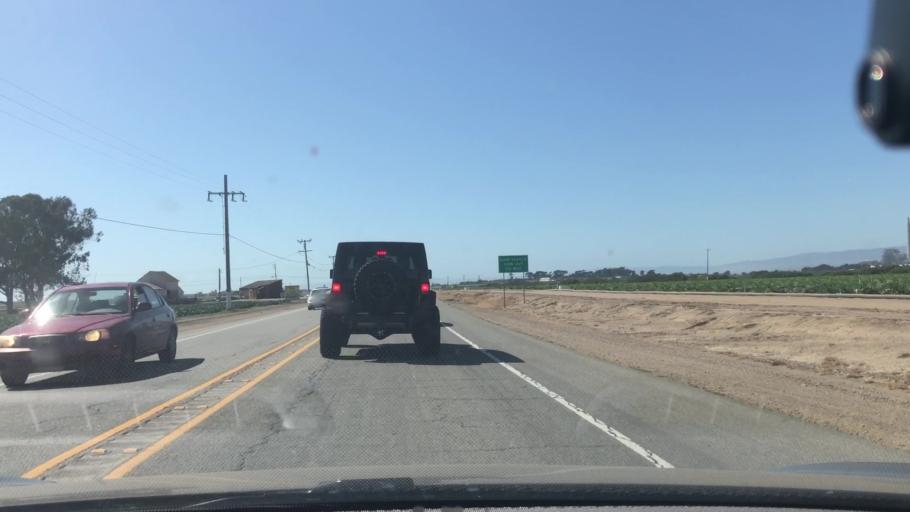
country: US
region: California
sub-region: Monterey County
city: Castroville
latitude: 36.7785
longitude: -121.7756
